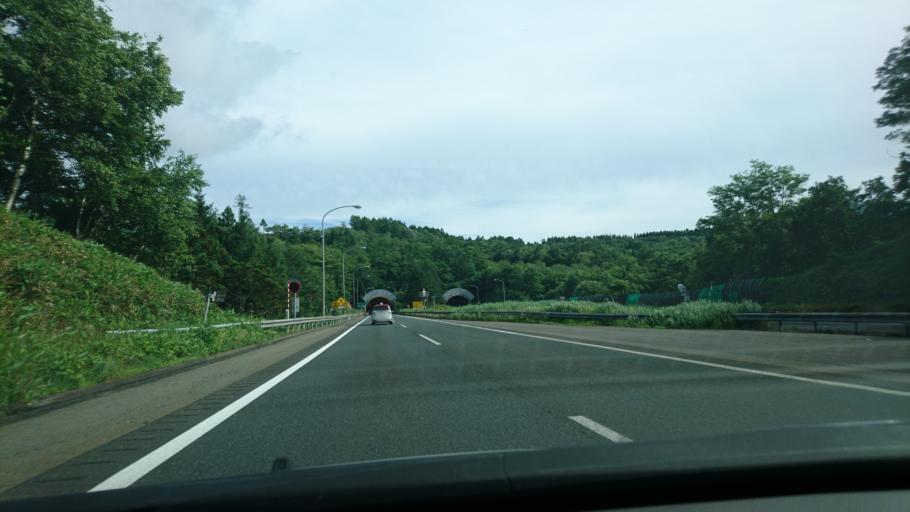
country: JP
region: Akita
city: Hanawa
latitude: 40.0220
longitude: 140.9839
